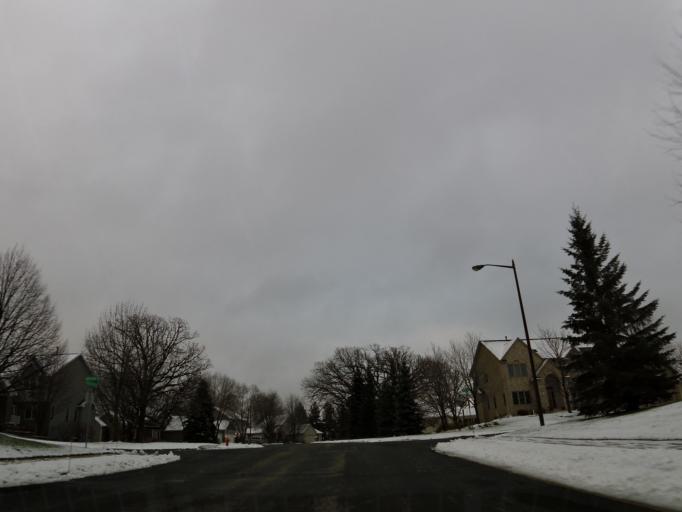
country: US
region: Minnesota
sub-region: Dakota County
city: Apple Valley
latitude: 44.7114
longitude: -93.2503
